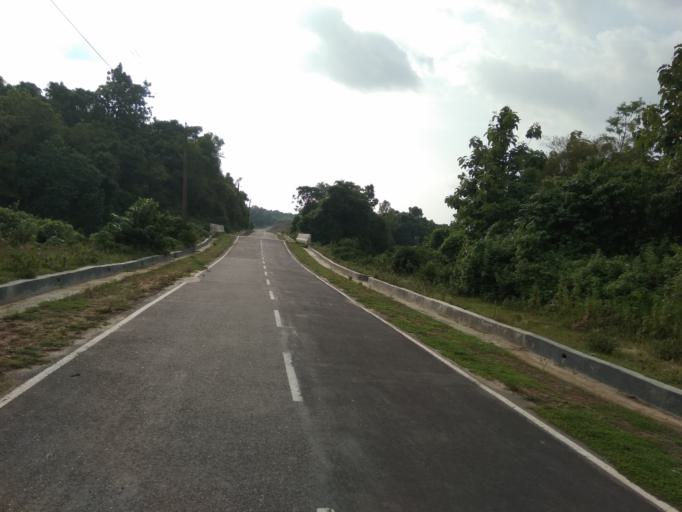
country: BD
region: Chittagong
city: Manikchari
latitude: 22.9361
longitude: 91.9083
